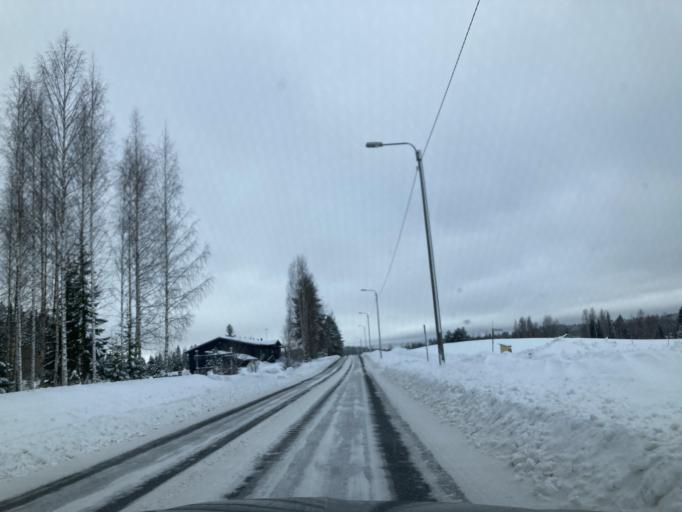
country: FI
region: Central Finland
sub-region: Jaemsae
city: Jaemsae
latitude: 61.8690
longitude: 25.2578
